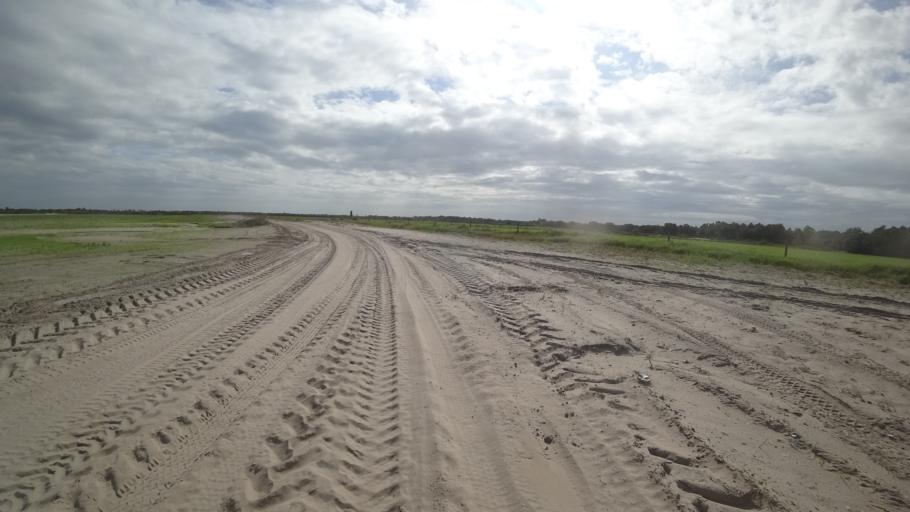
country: US
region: Florida
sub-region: Hillsborough County
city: Wimauma
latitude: 27.5647
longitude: -82.3111
